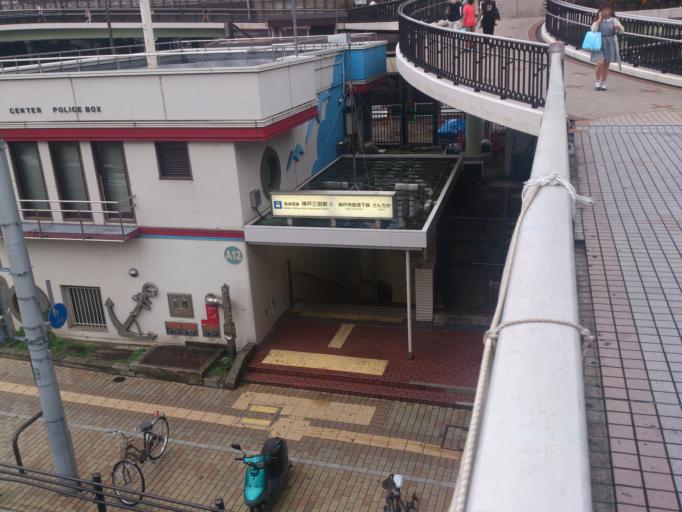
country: JP
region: Hyogo
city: Kobe
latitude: 34.6935
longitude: 135.1949
